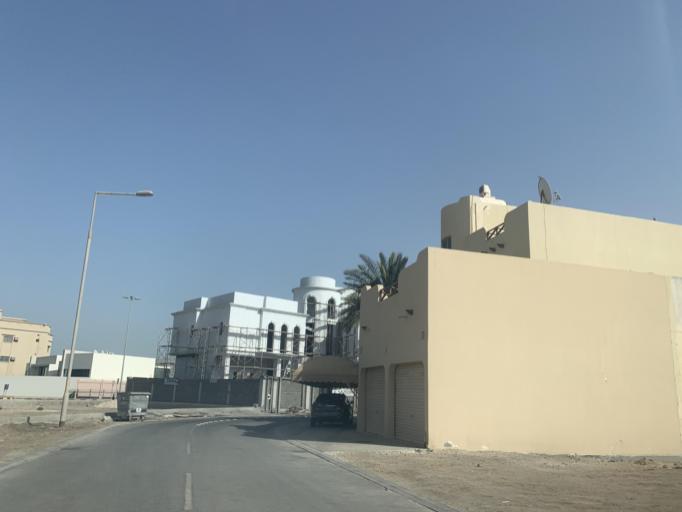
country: BH
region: Northern
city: Madinat `Isa
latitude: 26.1644
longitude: 50.5772
